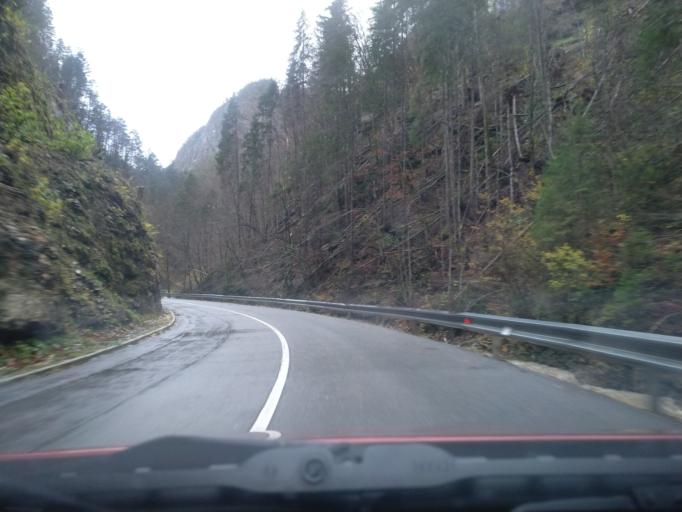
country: SI
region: Solcava
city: Solcava
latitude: 46.4244
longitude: 14.6618
